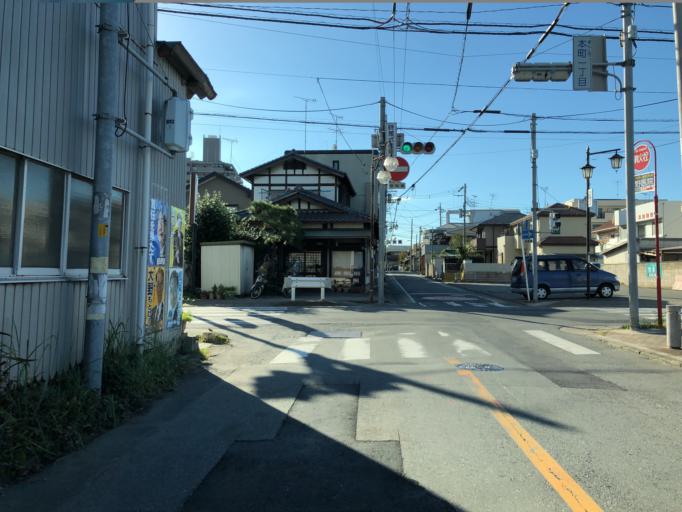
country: JP
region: Saitama
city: Fukiage-fujimi
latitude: 36.0408
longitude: 139.4061
